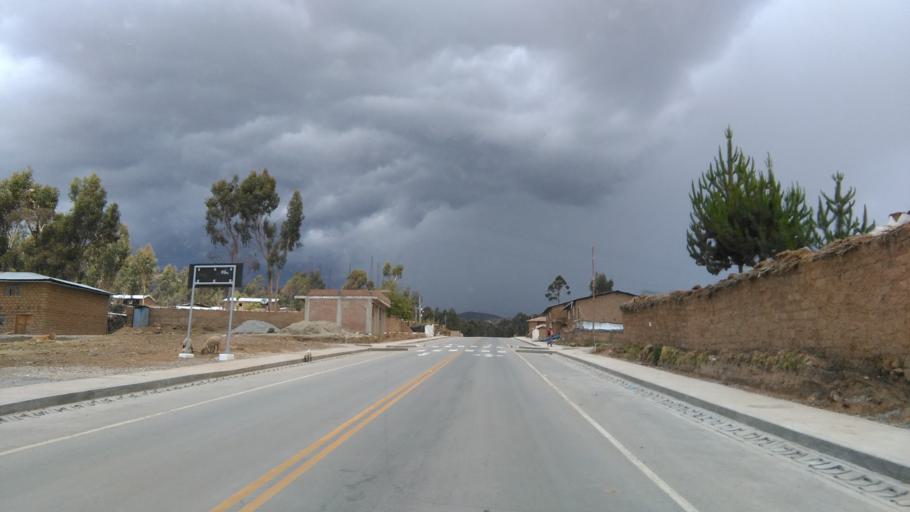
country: PE
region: Apurimac
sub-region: Provincia de Andahuaylas
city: San Jeronimo
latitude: -13.7293
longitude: -73.3531
